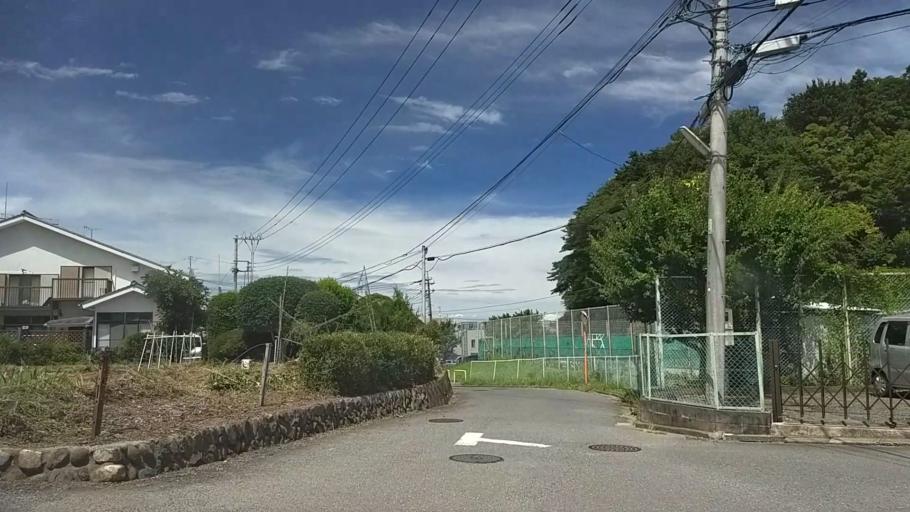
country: JP
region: Tokyo
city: Hachioji
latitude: 35.6424
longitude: 139.2971
